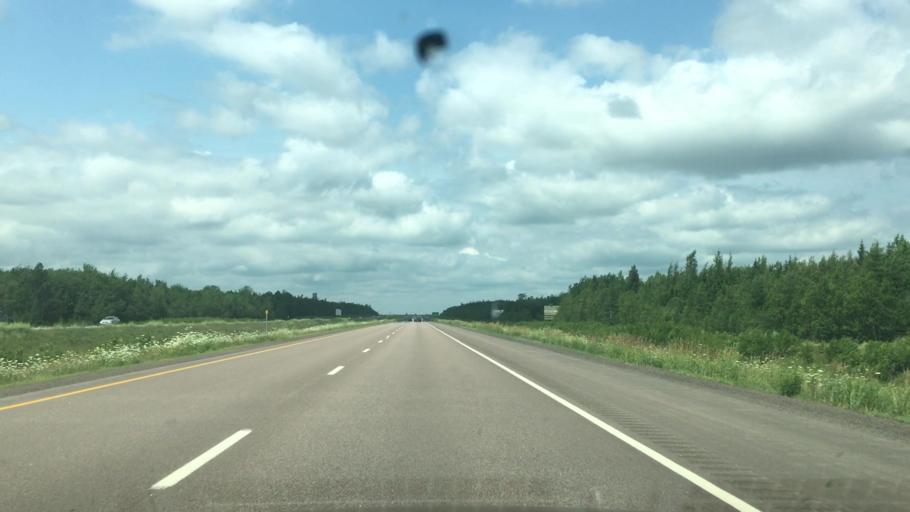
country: CA
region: New Brunswick
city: Dieppe
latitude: 46.1133
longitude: -64.6175
